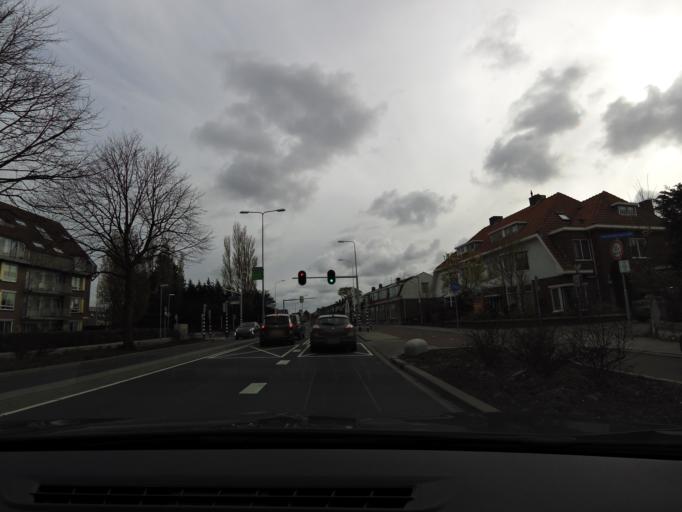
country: NL
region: South Holland
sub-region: Gemeente Hillegom
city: Hillegom
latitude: 52.2887
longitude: 4.5768
